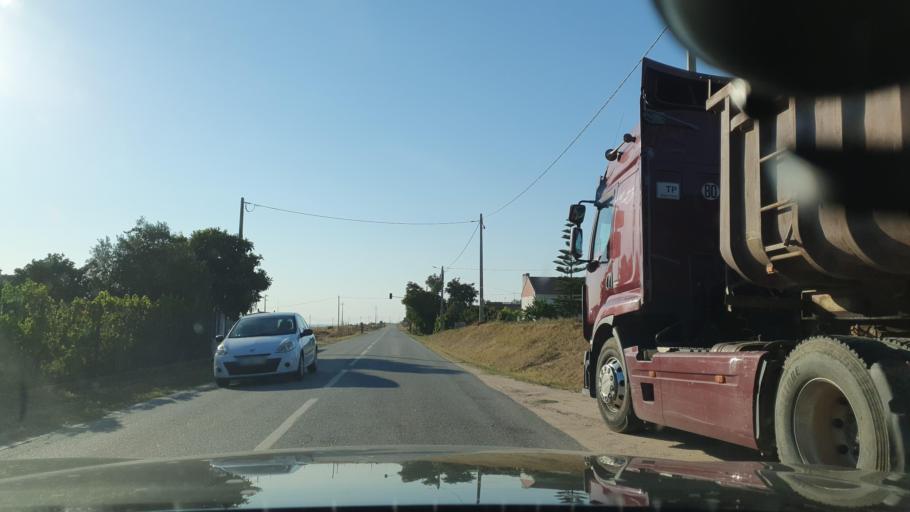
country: PT
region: Evora
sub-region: Estremoz
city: Estremoz
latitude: 38.8780
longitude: -7.6385
